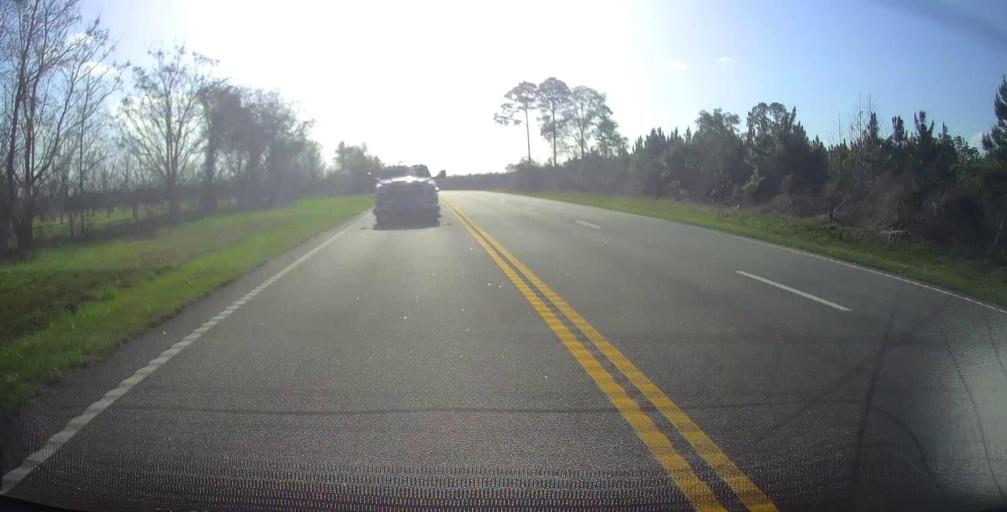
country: US
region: Georgia
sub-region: Montgomery County
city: Mount Vernon
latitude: 32.1895
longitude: -82.5251
